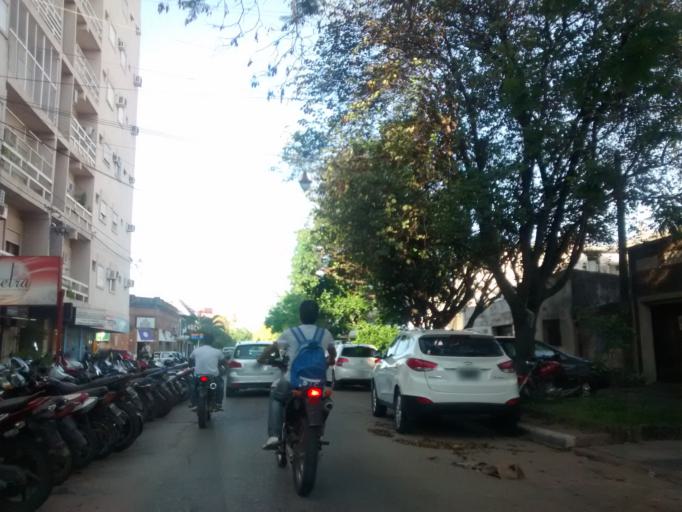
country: AR
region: Chaco
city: Resistencia
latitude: -27.4577
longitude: -58.9834
